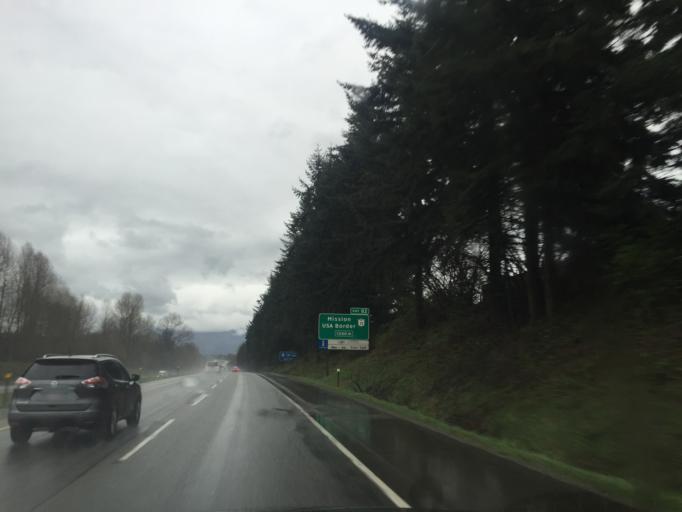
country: US
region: Washington
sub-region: Whatcom County
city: Sumas
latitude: 49.0334
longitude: -122.2820
